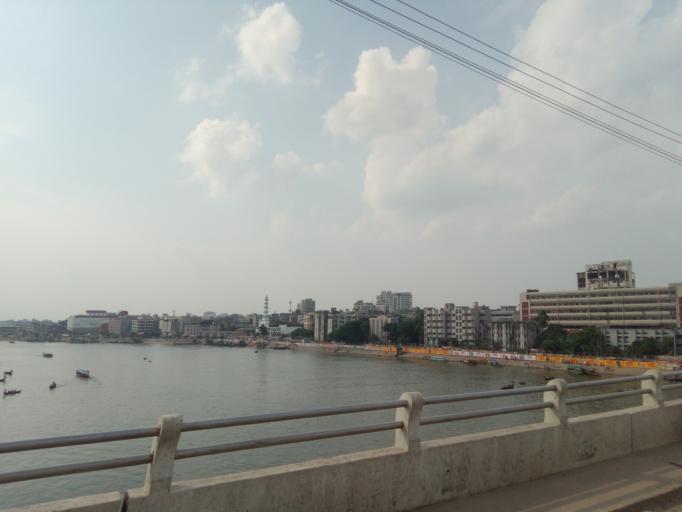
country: BD
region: Dhaka
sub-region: Dhaka
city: Dhaka
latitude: 23.7084
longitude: 90.4014
